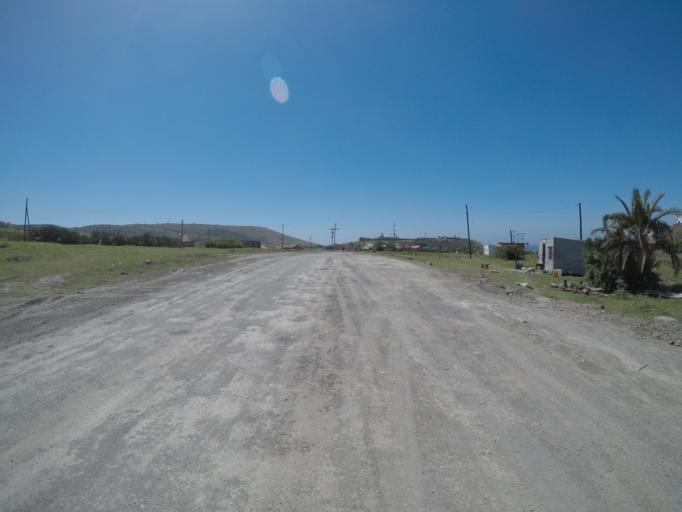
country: ZA
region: Eastern Cape
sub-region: OR Tambo District Municipality
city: Libode
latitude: -32.0312
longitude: 29.1071
